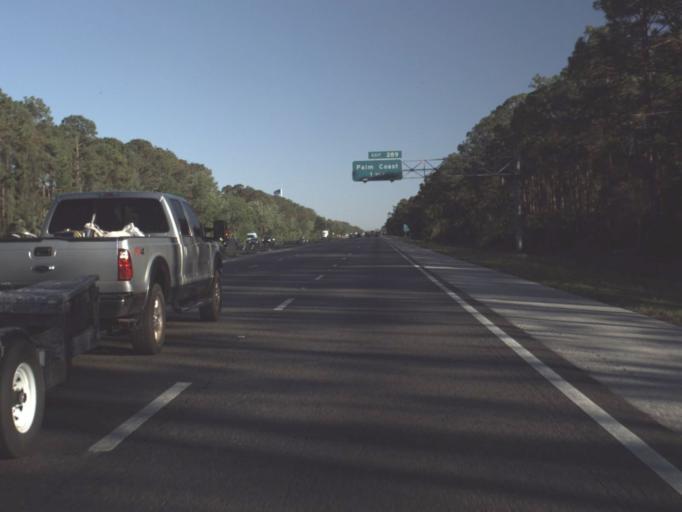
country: US
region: Florida
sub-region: Flagler County
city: Palm Coast
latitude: 29.5722
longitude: -81.2309
